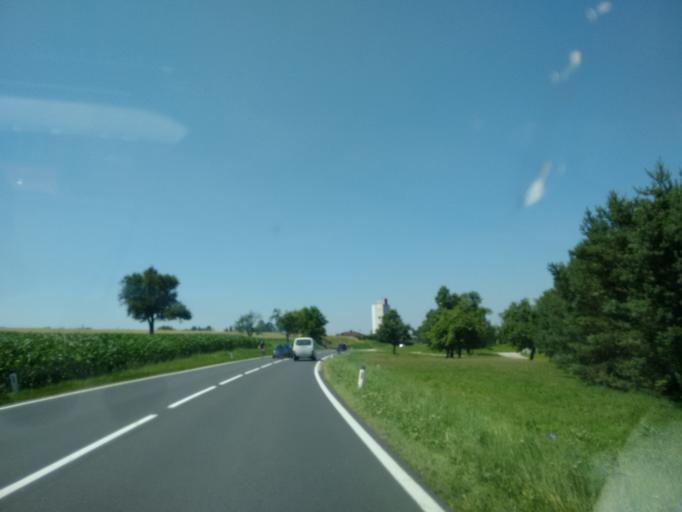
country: AT
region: Upper Austria
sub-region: Wels-Land
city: Buchkirchen
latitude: 48.2028
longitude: 13.9793
